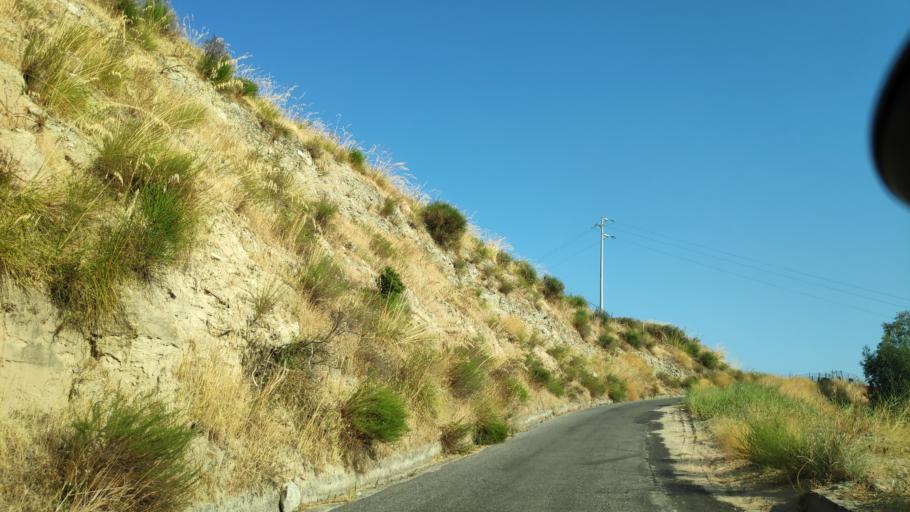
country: IT
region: Calabria
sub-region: Provincia di Catanzaro
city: Guardavalle
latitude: 38.5092
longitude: 16.5025
